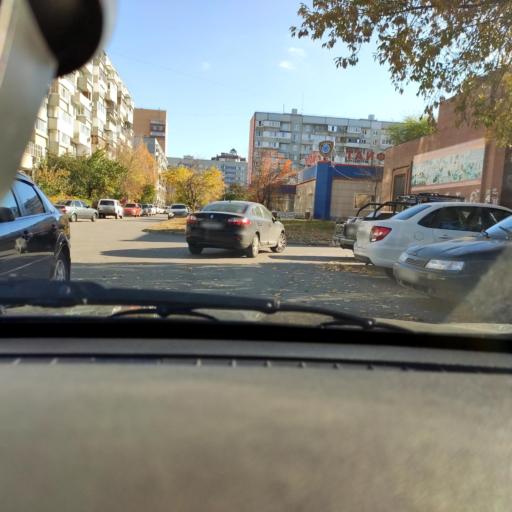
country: RU
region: Samara
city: Tol'yatti
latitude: 53.5340
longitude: 49.3384
